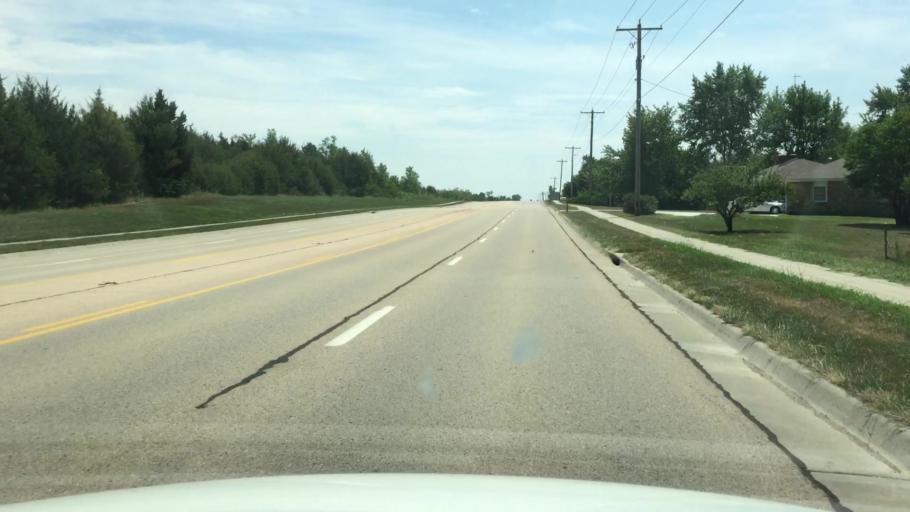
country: US
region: Kansas
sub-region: Shawnee County
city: Topeka
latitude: 38.9949
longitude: -95.6145
